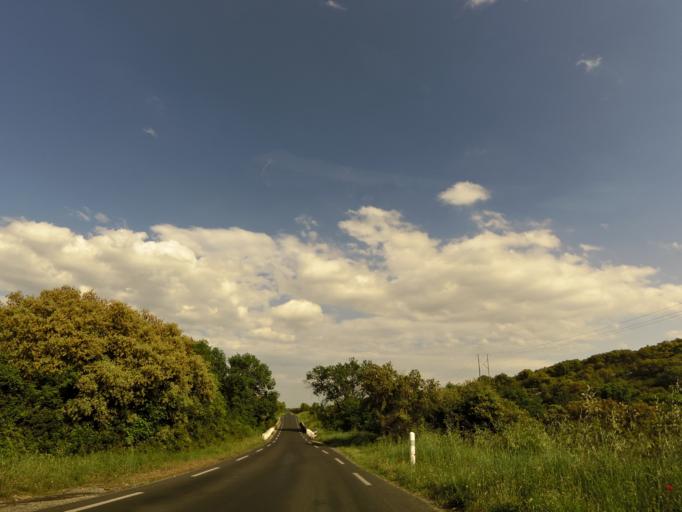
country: FR
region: Languedoc-Roussillon
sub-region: Departement du Gard
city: Aubais
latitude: 43.7544
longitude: 4.1133
